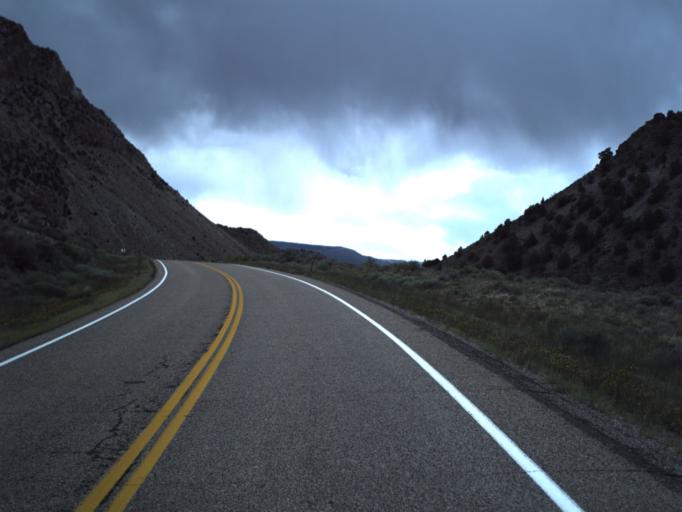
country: US
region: Utah
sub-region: Piute County
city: Junction
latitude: 38.1893
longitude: -112.1003
